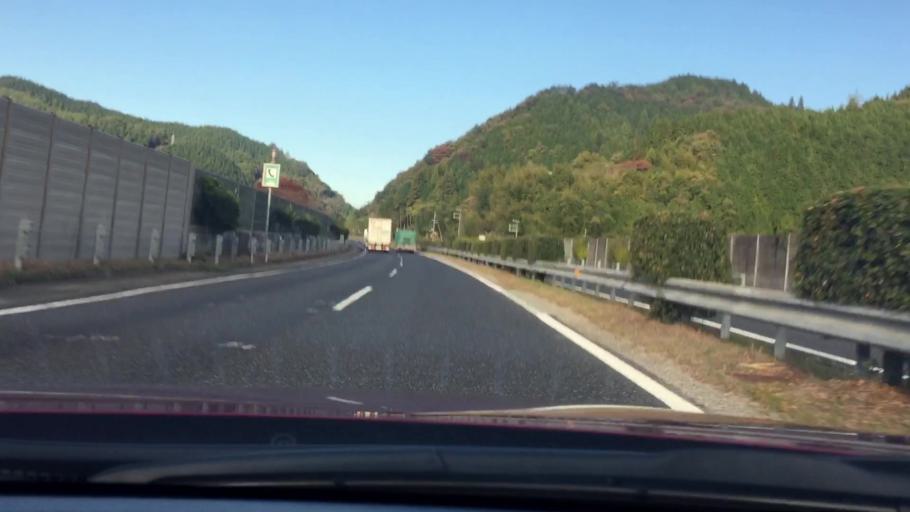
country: JP
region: Hyogo
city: Yamazakicho-nakabirose
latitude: 34.9781
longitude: 134.6320
